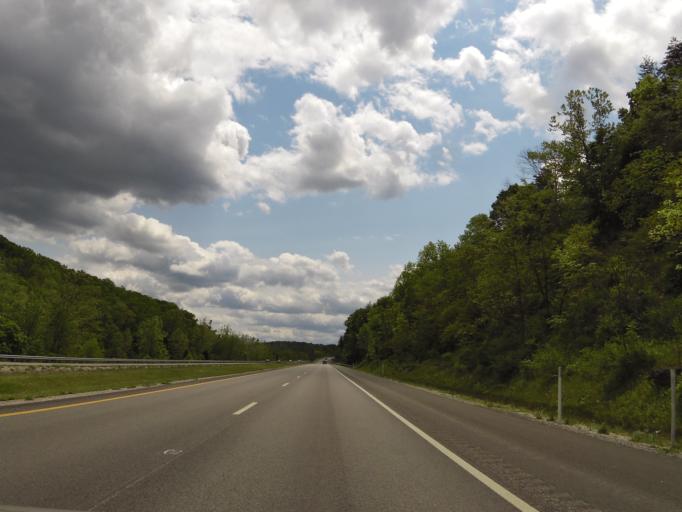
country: US
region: West Virginia
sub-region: Jackson County
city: Ripley
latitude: 38.6981
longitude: -81.6410
